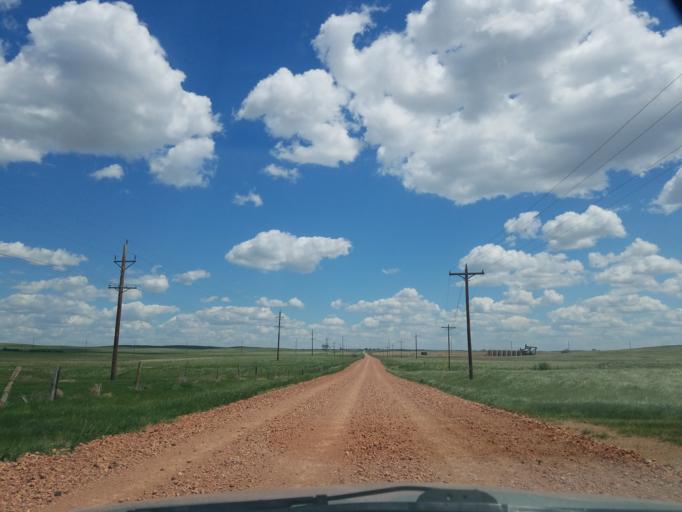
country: US
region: North Dakota
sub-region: McKenzie County
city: Watford City
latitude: 47.8194
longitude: -103.5942
